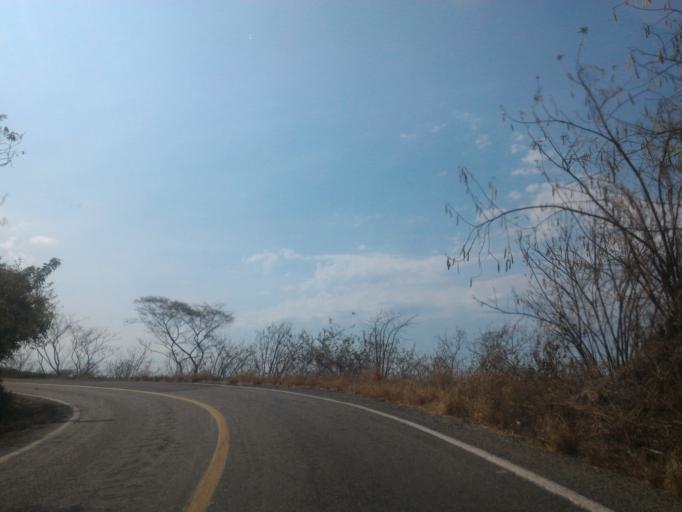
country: MX
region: Michoacan
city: Coahuayana Viejo
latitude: 18.4761
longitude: -103.5613
